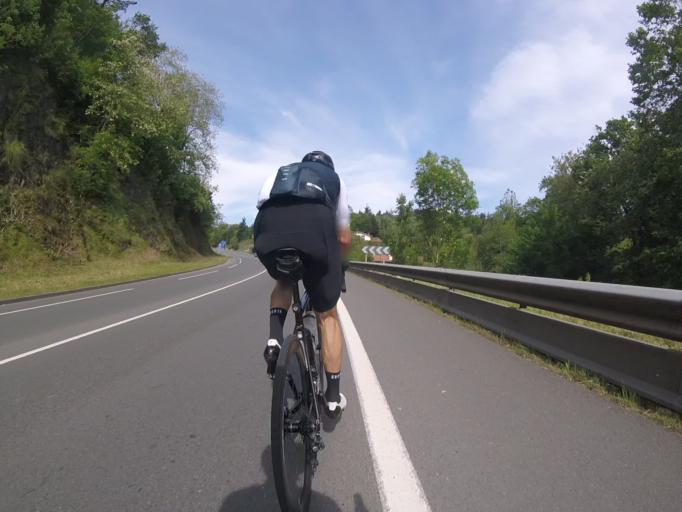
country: ES
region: Basque Country
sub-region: Provincia de Guipuzcoa
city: Cestona
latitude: 43.2550
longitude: -2.2626
